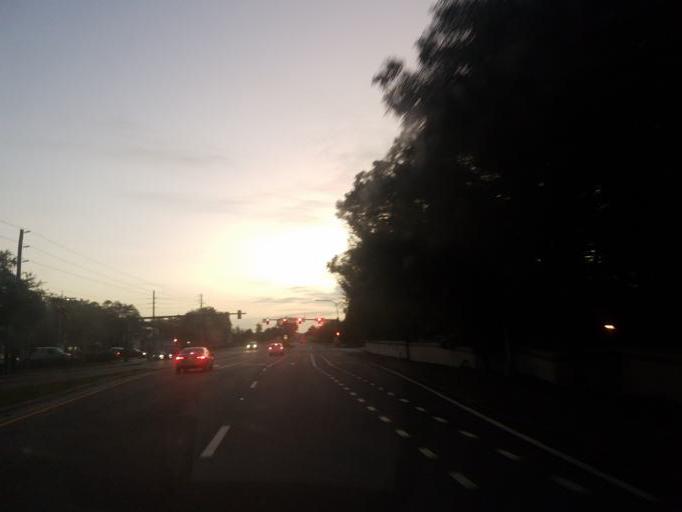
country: US
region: Florida
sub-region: Sarasota County
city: Lake Sarasota
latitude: 27.2838
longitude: -82.4532
